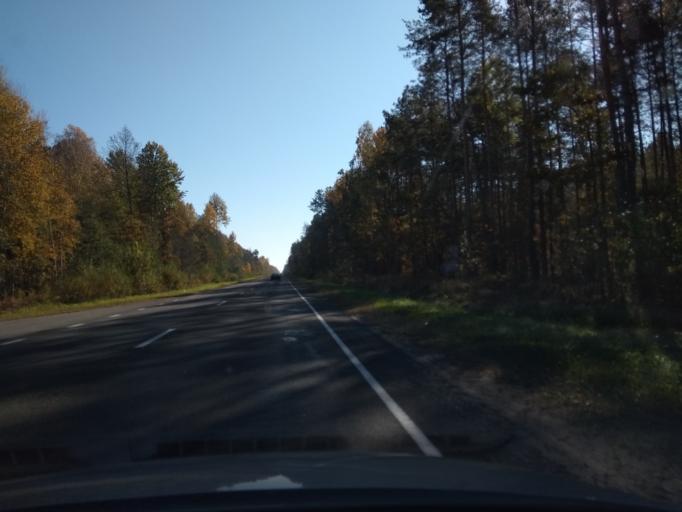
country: BY
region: Brest
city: Malaryta
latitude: 51.9051
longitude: 24.1139
